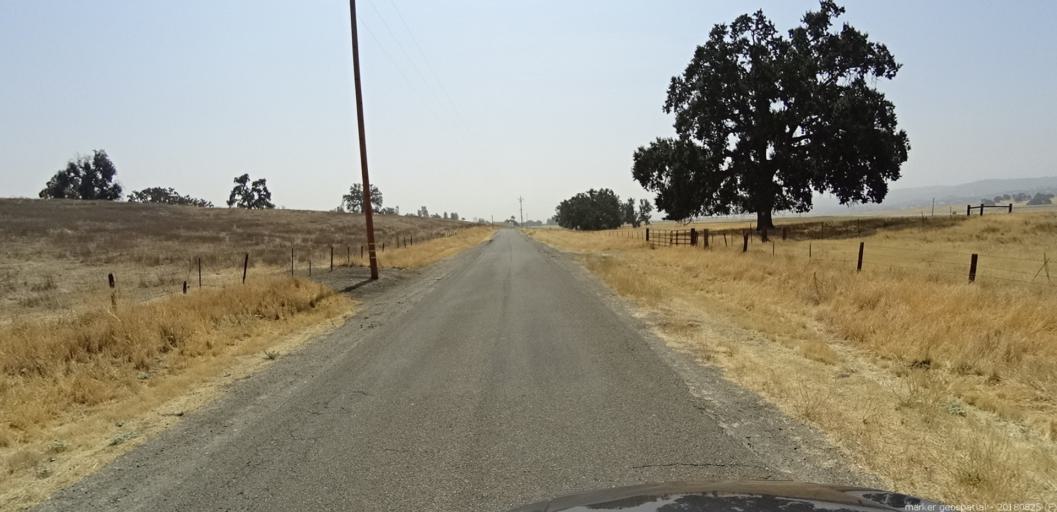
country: US
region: California
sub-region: San Luis Obispo County
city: Shandon
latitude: 35.8555
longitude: -120.3887
